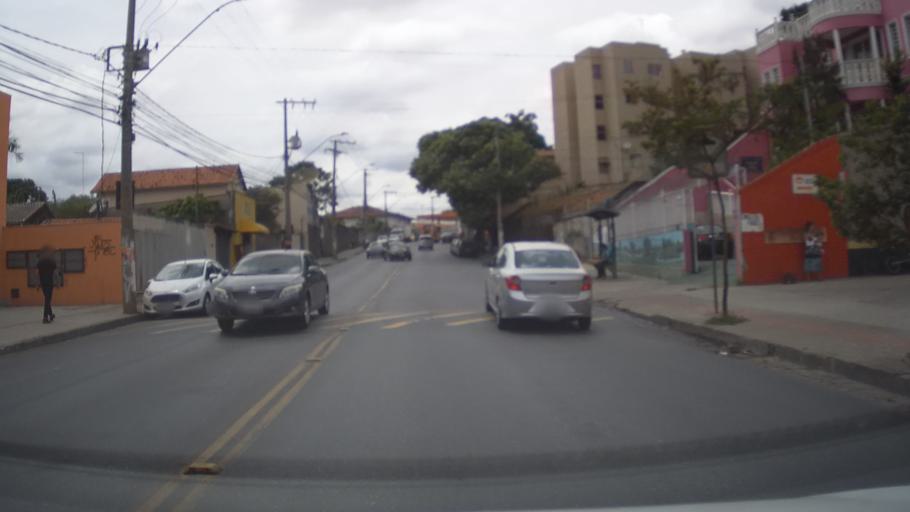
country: BR
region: Minas Gerais
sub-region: Belo Horizonte
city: Belo Horizonte
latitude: -19.8107
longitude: -43.9671
